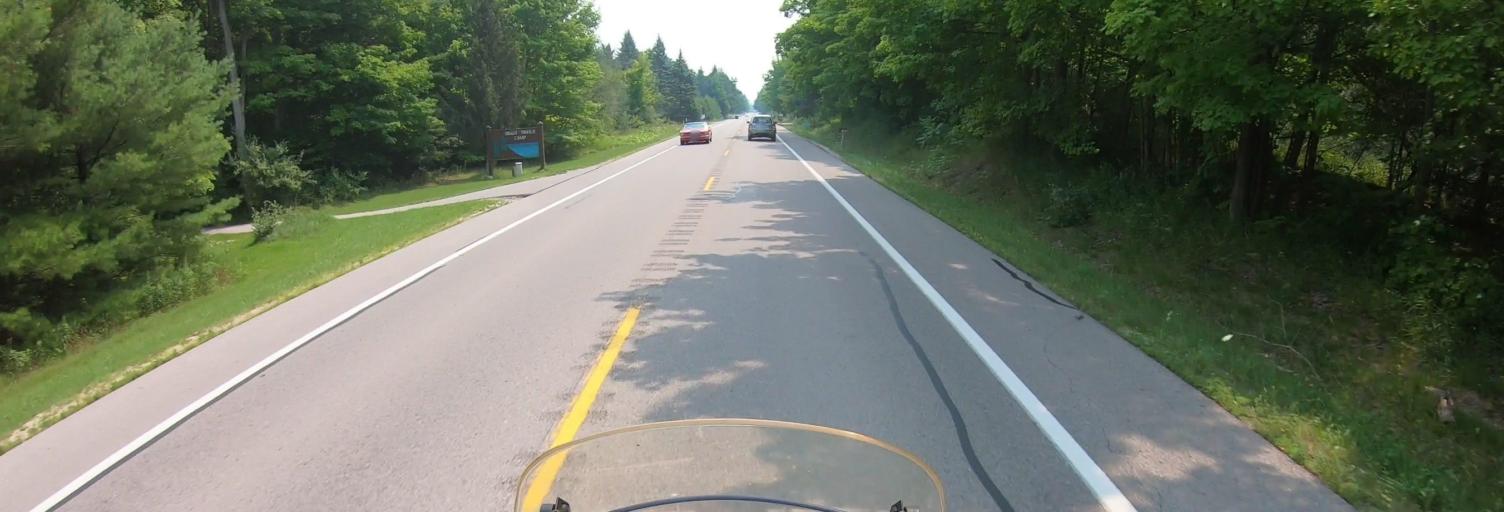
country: US
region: Michigan
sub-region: Leelanau County
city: Leland
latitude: 45.0809
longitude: -85.5936
